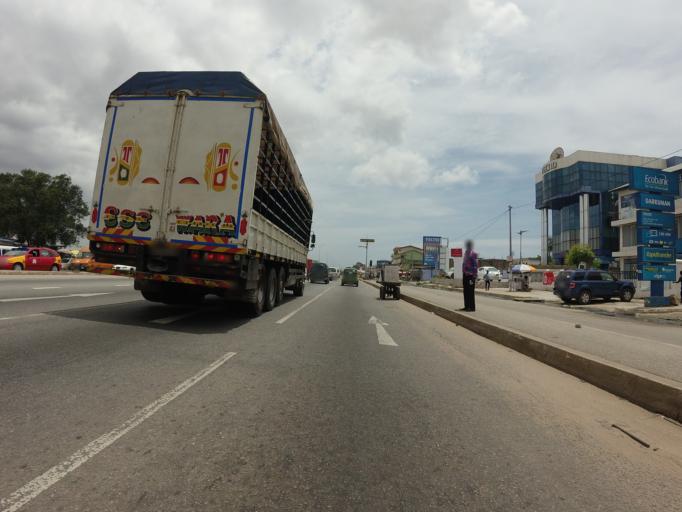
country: GH
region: Greater Accra
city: Gbawe
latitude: 5.5770
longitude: -0.2556
